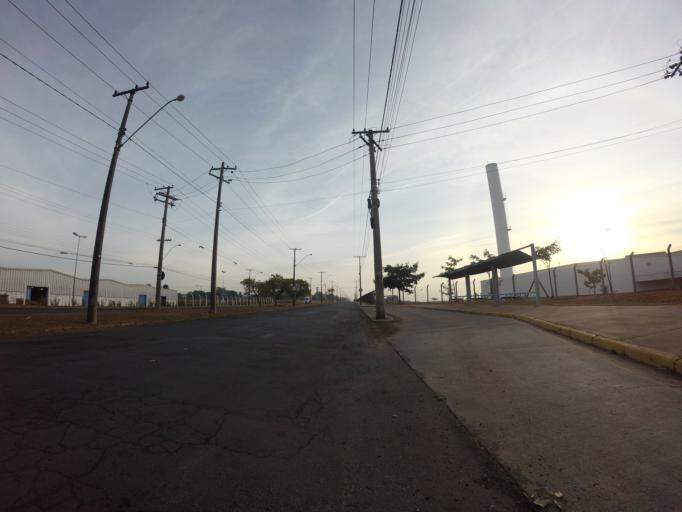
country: BR
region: Sao Paulo
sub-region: Piracicaba
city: Piracicaba
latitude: -22.7348
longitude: -47.5887
